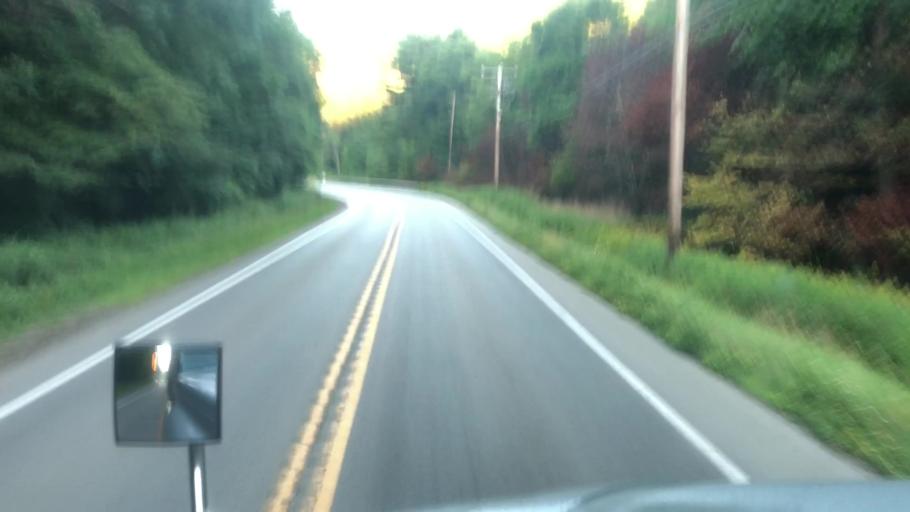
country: US
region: Pennsylvania
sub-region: Venango County
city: Hasson Heights
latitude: 41.4827
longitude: -79.6726
